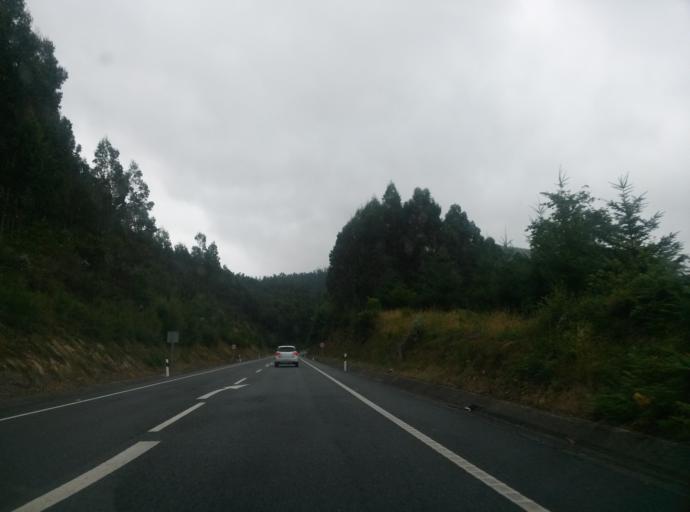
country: ES
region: Galicia
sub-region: Provincia de Lugo
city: Viveiro
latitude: 43.5852
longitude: -7.6308
